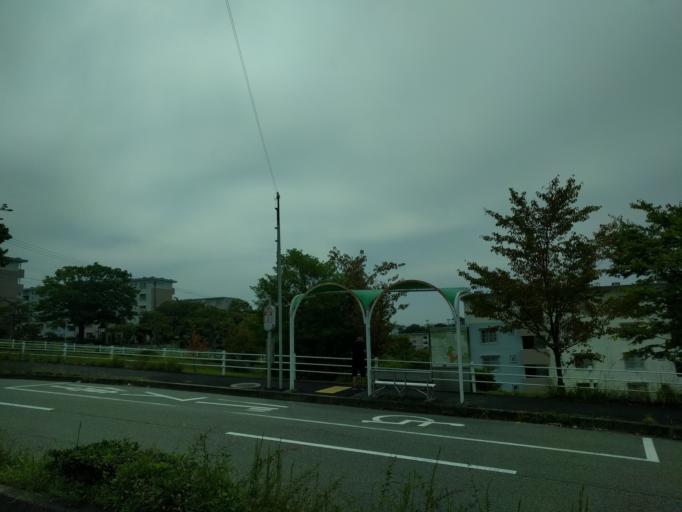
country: JP
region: Hyogo
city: Kobe
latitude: 34.6961
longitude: 135.1242
